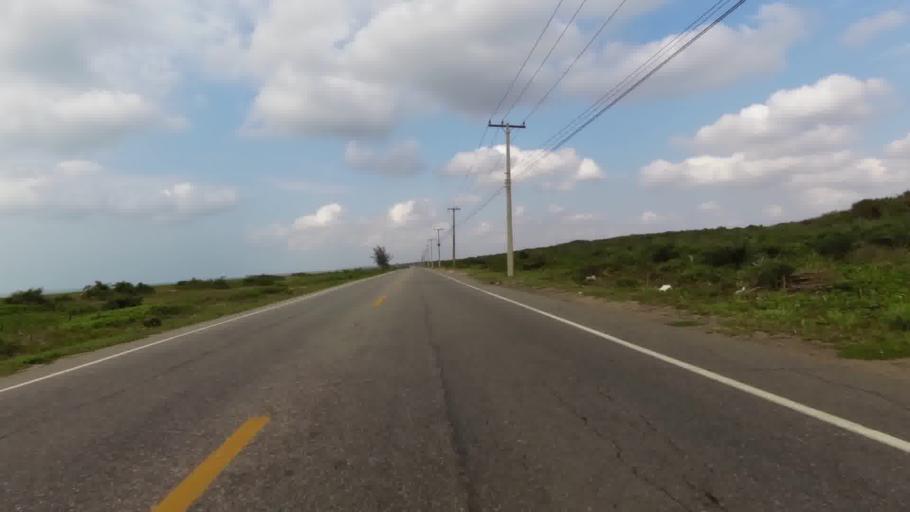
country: BR
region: Espirito Santo
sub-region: Itapemirim
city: Itapemirim
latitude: -20.9466
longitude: -40.8059
